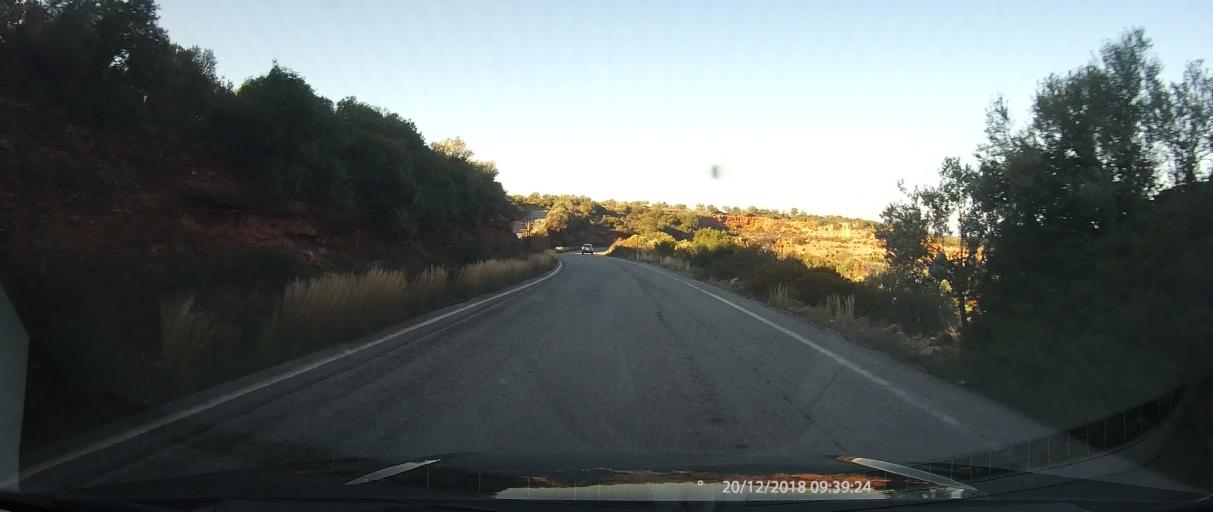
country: GR
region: Peloponnese
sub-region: Nomos Lakonias
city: Yerakion
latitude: 36.9396
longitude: 22.7766
